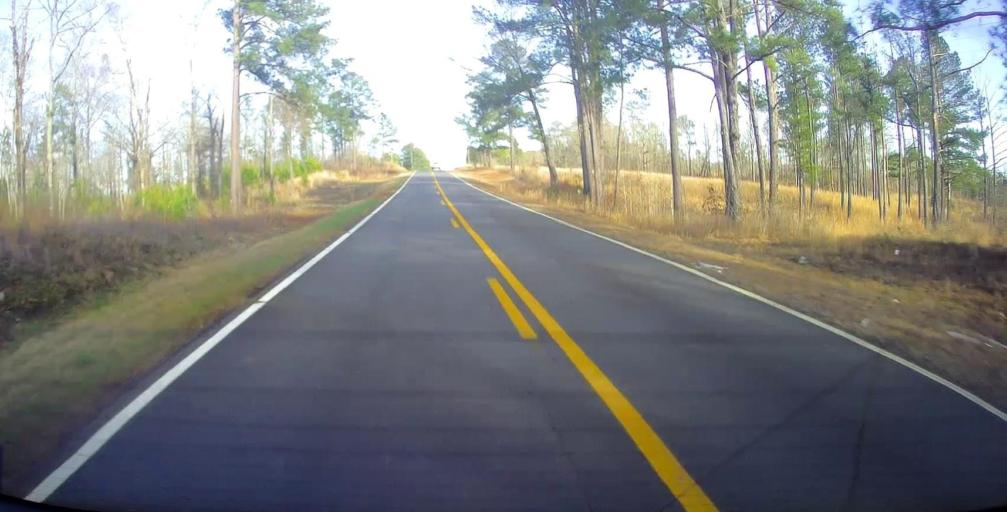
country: US
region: Georgia
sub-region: Crawford County
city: Knoxville
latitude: 32.8240
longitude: -83.9588
